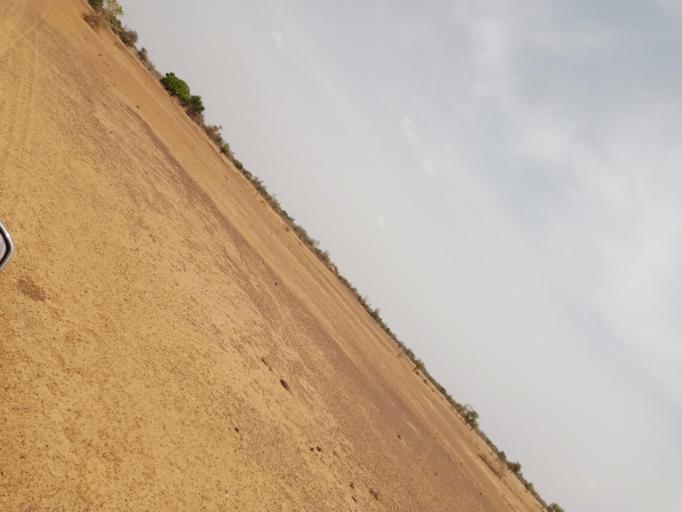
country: BF
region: Est
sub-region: Gnagna Province
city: Bogande
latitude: 13.0949
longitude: -0.0364
